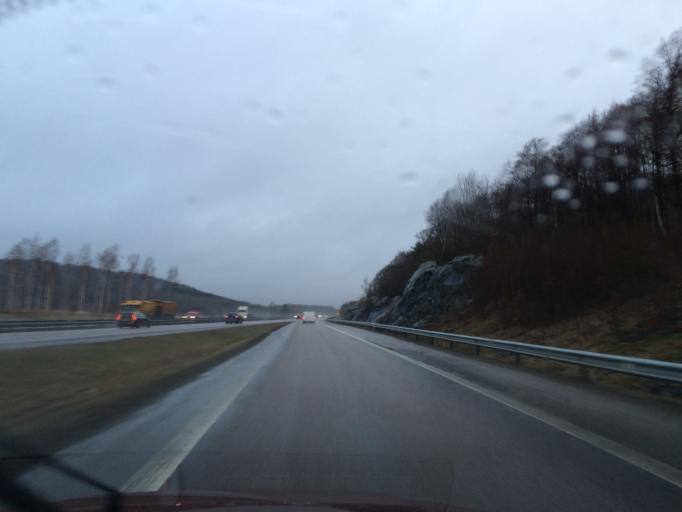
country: SE
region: Halland
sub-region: Kungsbacka Kommun
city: Kungsbacka
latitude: 57.5128
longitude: 12.0522
